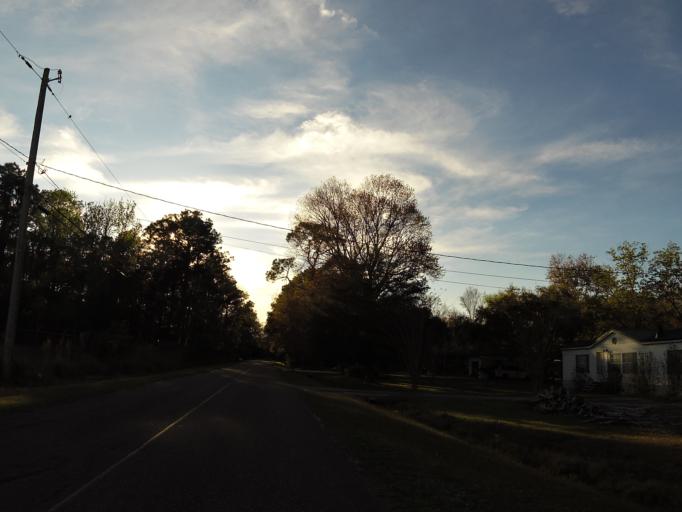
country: US
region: Florida
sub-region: Duval County
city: Jacksonville
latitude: 30.4626
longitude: -81.6434
